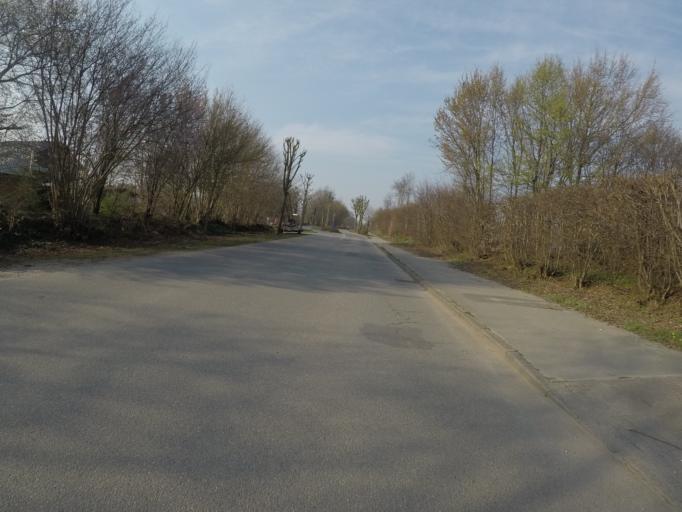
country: DE
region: Schleswig-Holstein
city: Kukels
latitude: 53.9028
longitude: 10.2320
